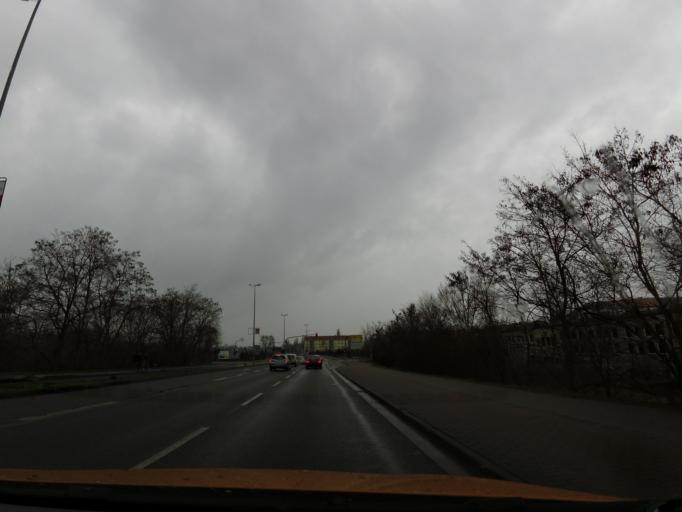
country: DE
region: Brandenburg
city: Brandenburg an der Havel
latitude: 52.4056
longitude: 12.5375
